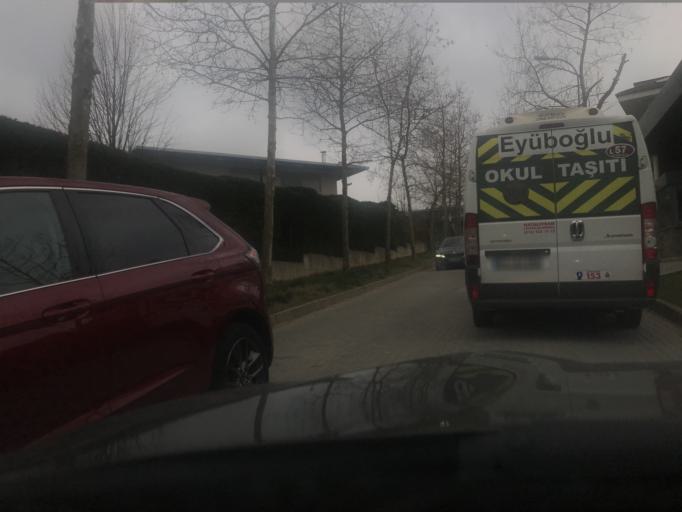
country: TR
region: Istanbul
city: Umraniye
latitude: 41.0444
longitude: 29.1623
